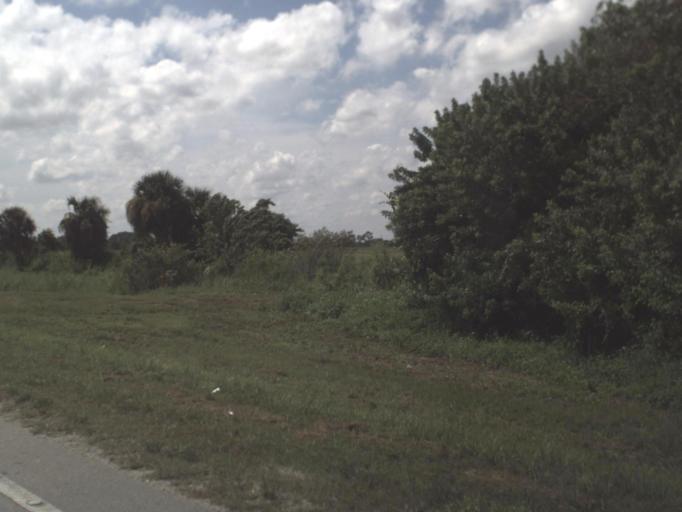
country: US
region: Florida
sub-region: Collier County
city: Immokalee
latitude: 26.4743
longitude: -81.4345
